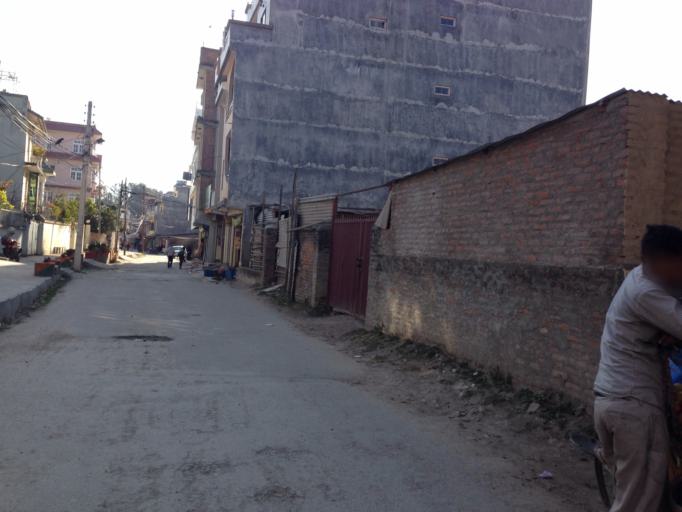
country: NP
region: Central Region
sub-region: Bagmati Zone
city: Kathmandu
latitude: 27.7248
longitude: 85.3345
